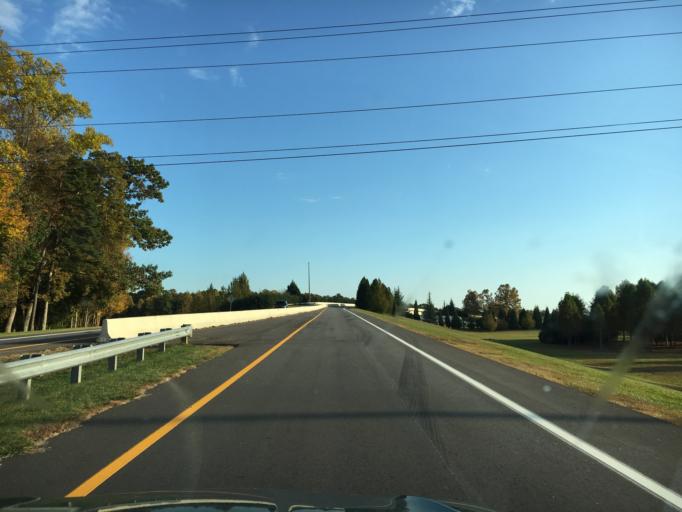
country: US
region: South Carolina
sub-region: Greenville County
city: Greer
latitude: 34.8795
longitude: -82.2144
